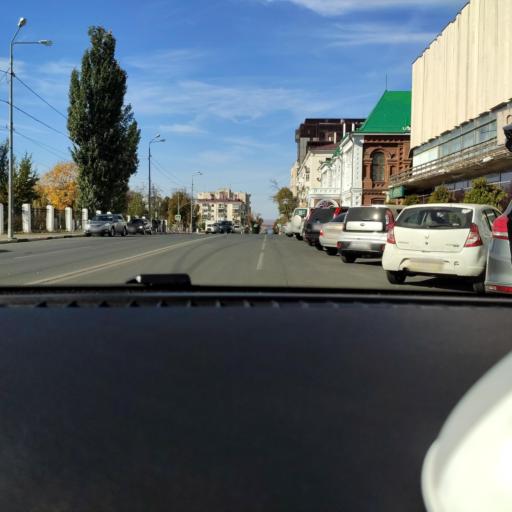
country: RU
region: Samara
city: Samara
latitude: 53.1973
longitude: 50.1050
